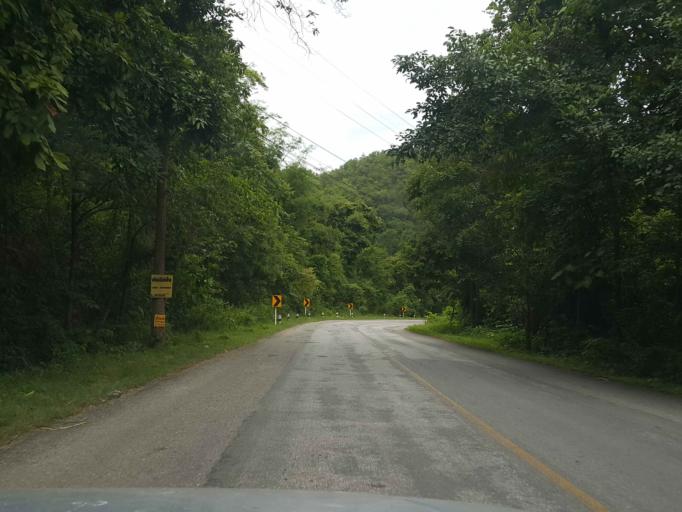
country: TH
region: Lampang
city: Thoen
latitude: 17.6349
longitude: 99.3106
